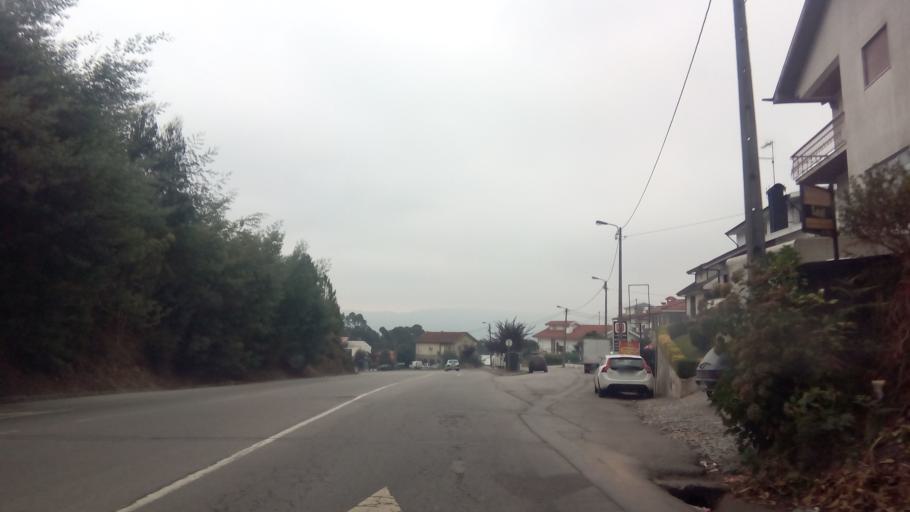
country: PT
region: Porto
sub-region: Paredes
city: Madalena
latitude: 41.2185
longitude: -8.3609
